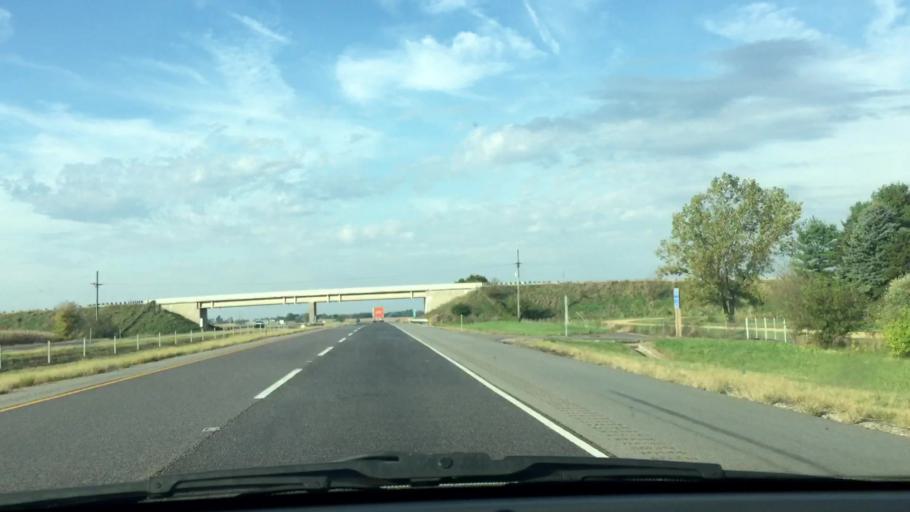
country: US
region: Illinois
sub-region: Lee County
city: Franklin Grove
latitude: 41.8354
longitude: -89.2732
